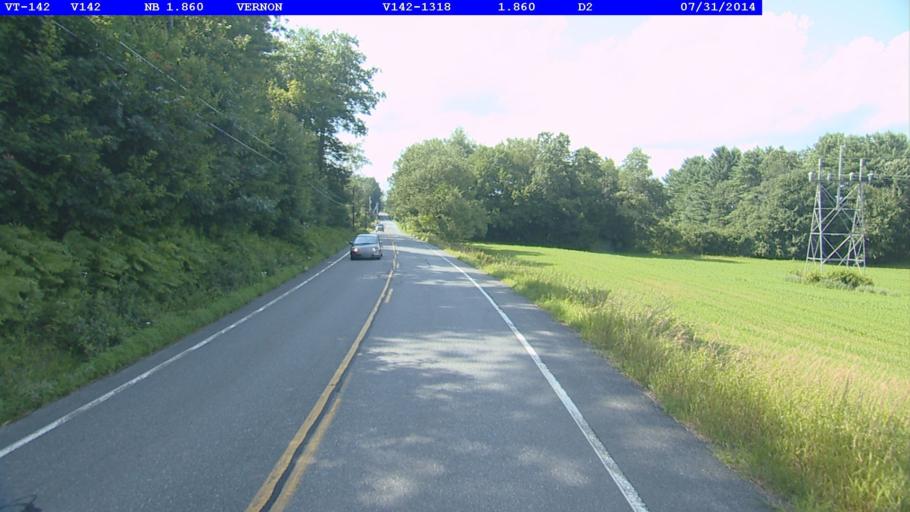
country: US
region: New Hampshire
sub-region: Cheshire County
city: Hinsdale
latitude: 42.7510
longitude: -72.4795
